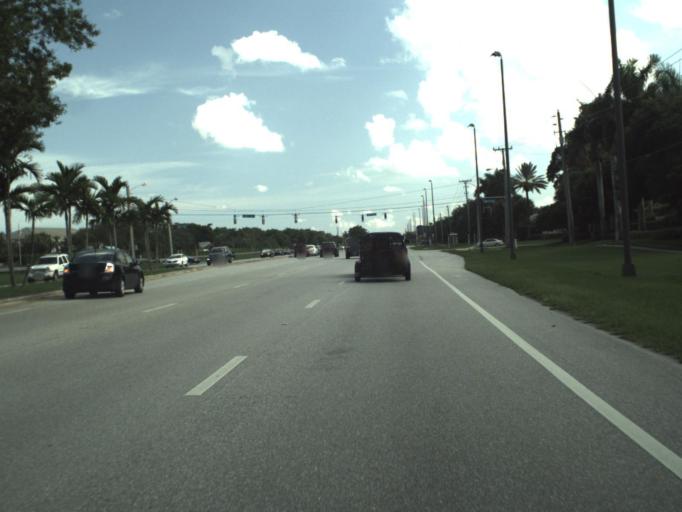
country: US
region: Florida
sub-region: Palm Beach County
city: Boca Pointe
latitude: 26.3471
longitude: -80.2034
